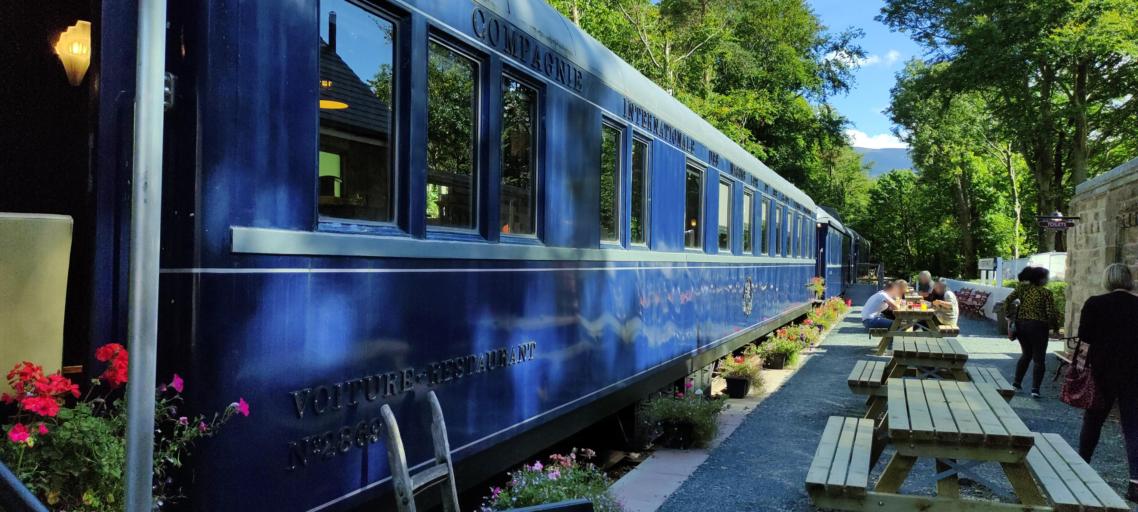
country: GB
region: England
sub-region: Cumbria
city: Cockermouth
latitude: 54.6677
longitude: -3.2436
